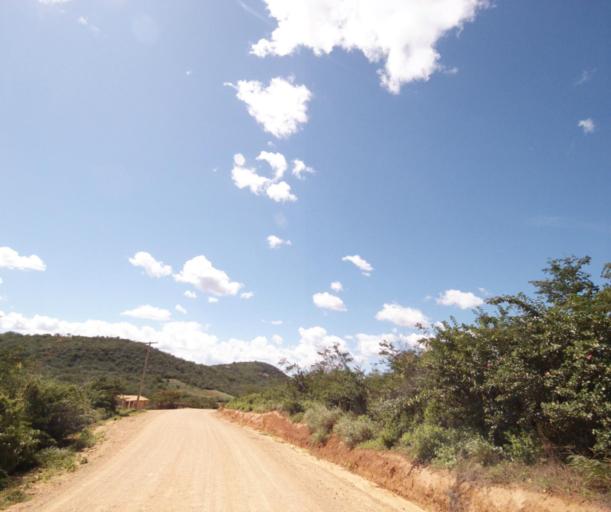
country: BR
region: Bahia
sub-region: Pocoes
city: Pocoes
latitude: -14.2683
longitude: -40.6954
